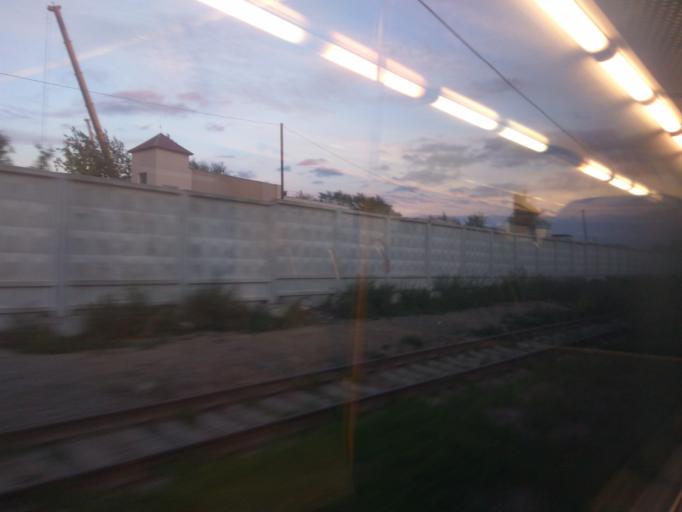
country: RU
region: Moscow
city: Solntsevo
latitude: 55.6480
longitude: 37.3799
